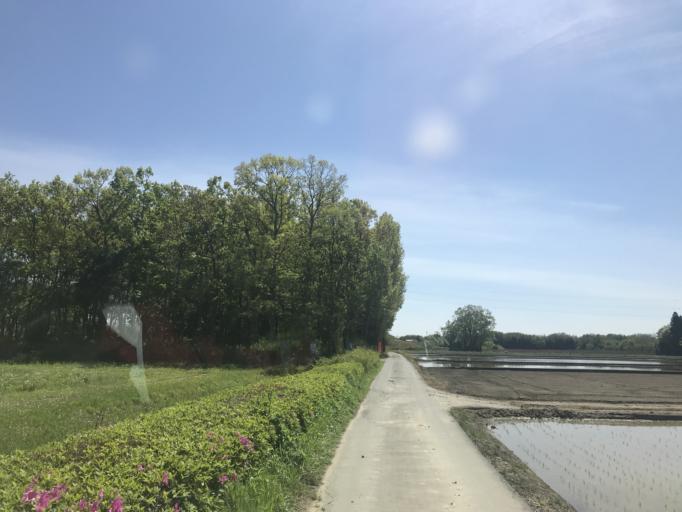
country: JP
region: Ibaraki
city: Mitsukaido
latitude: 36.0144
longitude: 139.9804
